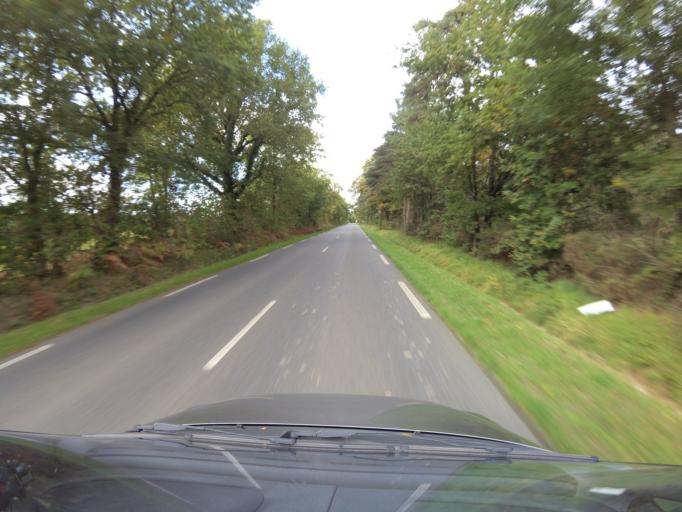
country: FR
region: Pays de la Loire
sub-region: Departement de la Loire-Atlantique
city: Plesse
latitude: 47.5018
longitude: -1.8696
